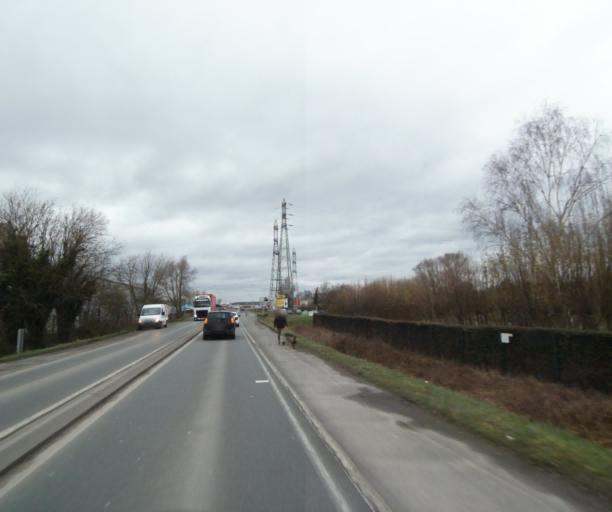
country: FR
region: Nord-Pas-de-Calais
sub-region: Departement du Nord
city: Saint-Saulve
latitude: 50.3834
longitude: 3.5569
